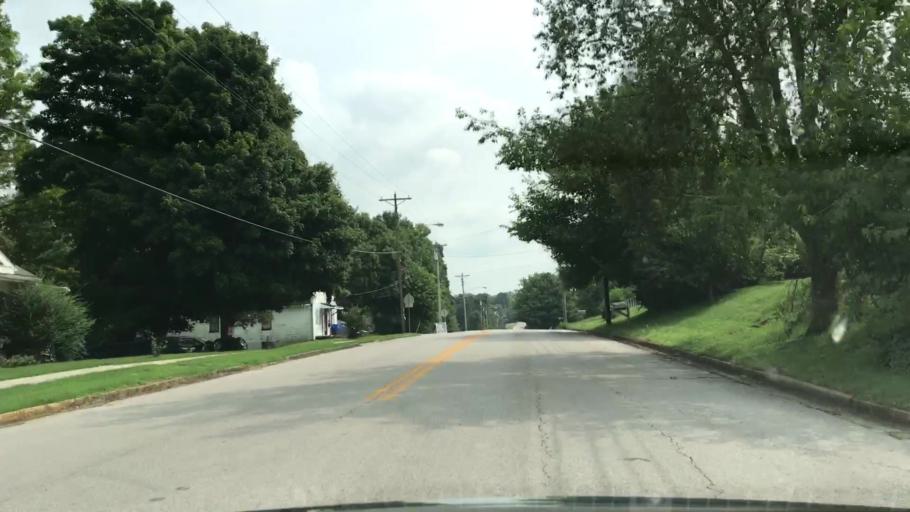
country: US
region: Kentucky
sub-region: Barren County
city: Cave City
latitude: 37.0944
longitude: -86.0453
